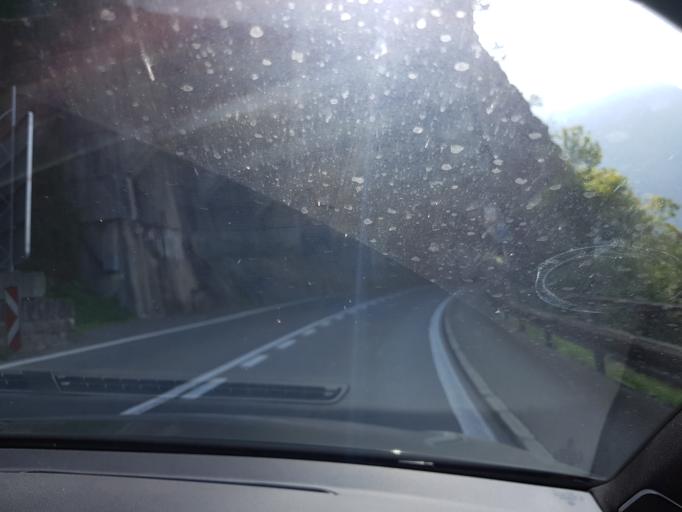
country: CH
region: Uri
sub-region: Uri
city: Bauen
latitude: 46.9558
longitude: 8.6193
